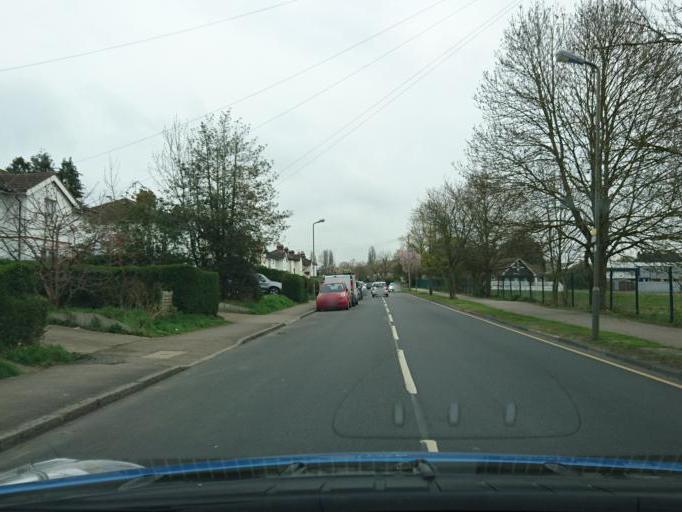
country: GB
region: England
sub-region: Greater London
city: Barnet
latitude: 51.6444
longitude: -0.1940
